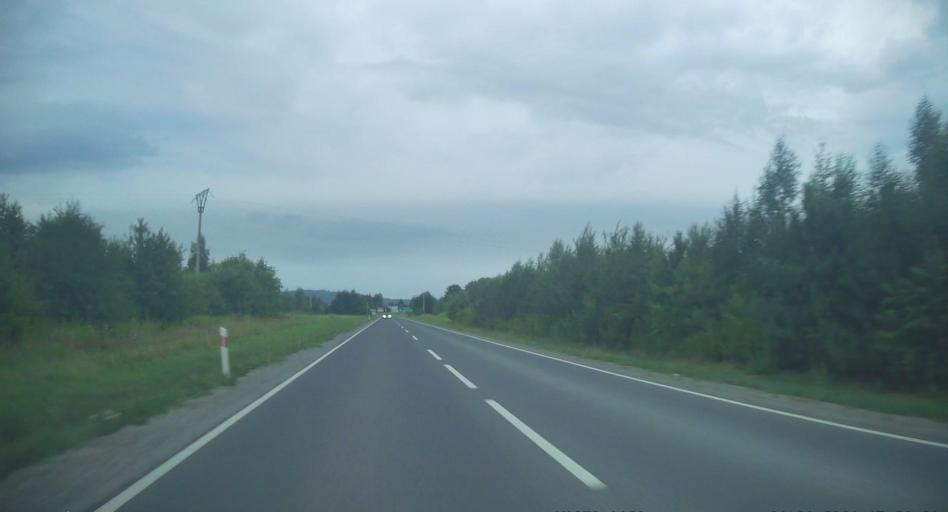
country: PL
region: Lesser Poland Voivodeship
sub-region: Powiat tarnowski
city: Wojnicz
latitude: 49.9784
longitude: 20.8417
